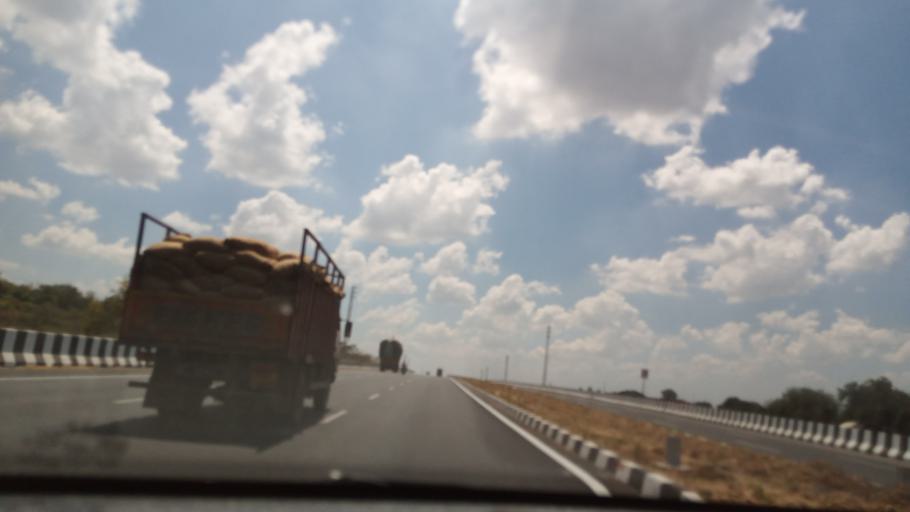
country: IN
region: Andhra Pradesh
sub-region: Chittoor
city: Pakala
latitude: 13.4546
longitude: 79.1630
